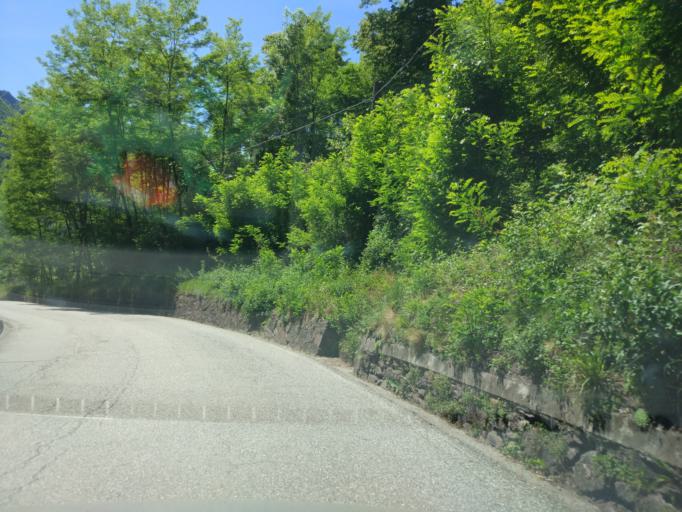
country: IT
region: Lombardy
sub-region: Provincia di Lecco
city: Taceno
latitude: 46.0245
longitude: 9.3678
